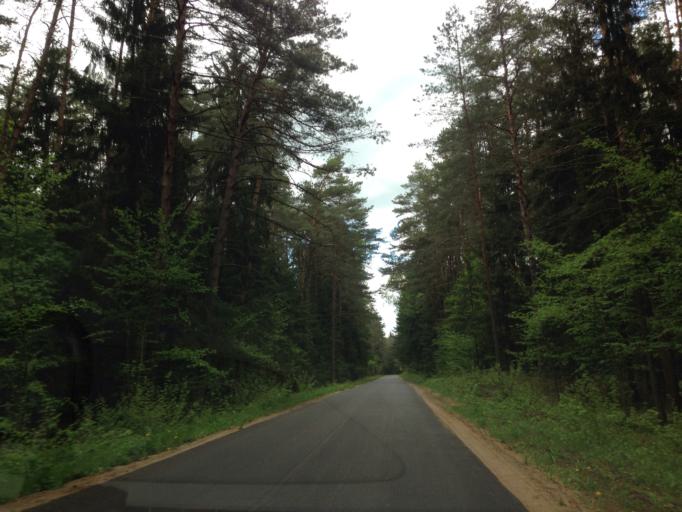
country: PL
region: Podlasie
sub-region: Powiat moniecki
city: Goniadz
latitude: 53.3571
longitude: 22.5992
